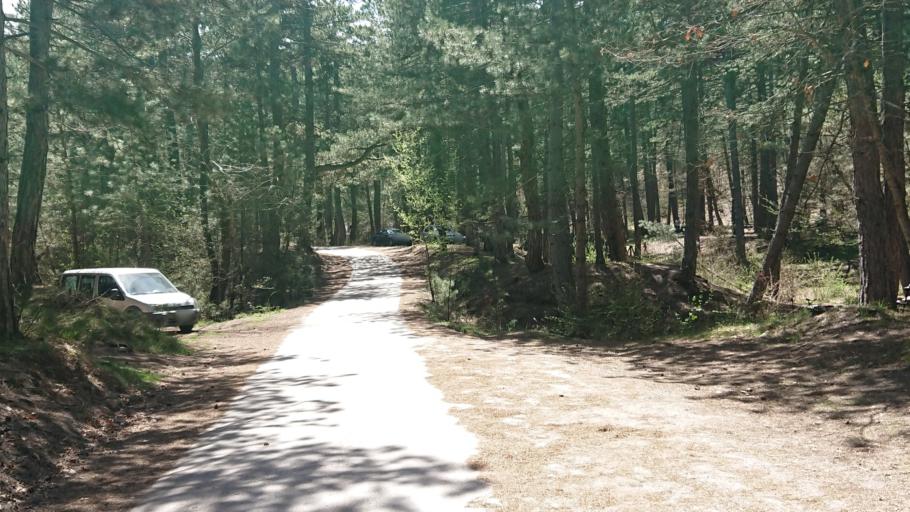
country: TR
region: Kuetahya
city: Sabuncu
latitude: 39.5122
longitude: 30.4234
